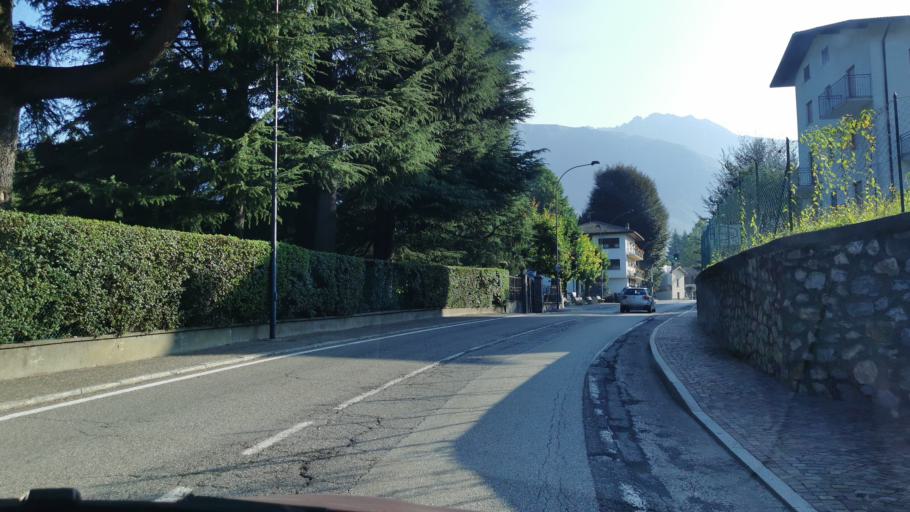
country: IT
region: Lombardy
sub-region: Provincia di Lecco
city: Cremeno
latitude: 45.9271
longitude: 9.4589
